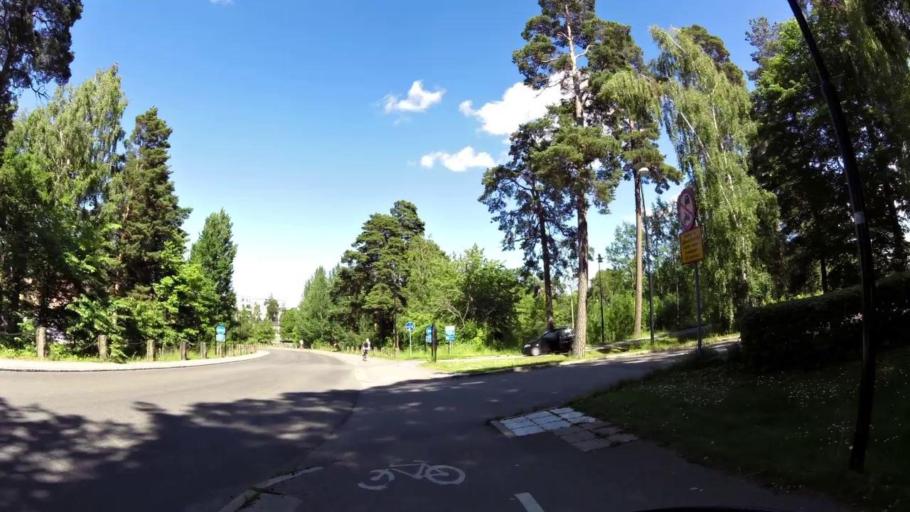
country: SE
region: OEstergoetland
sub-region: Linkopings Kommun
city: Linkoping
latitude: 58.3978
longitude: 15.6188
